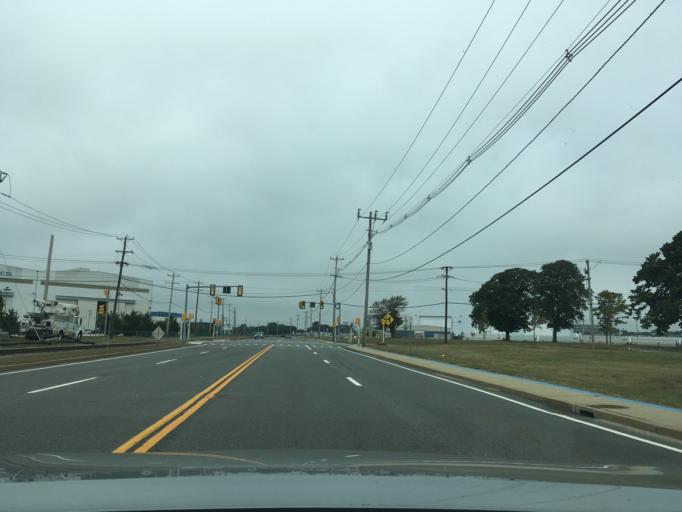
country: US
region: Rhode Island
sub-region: Washington County
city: North Kingstown
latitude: 41.5897
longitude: -71.4206
